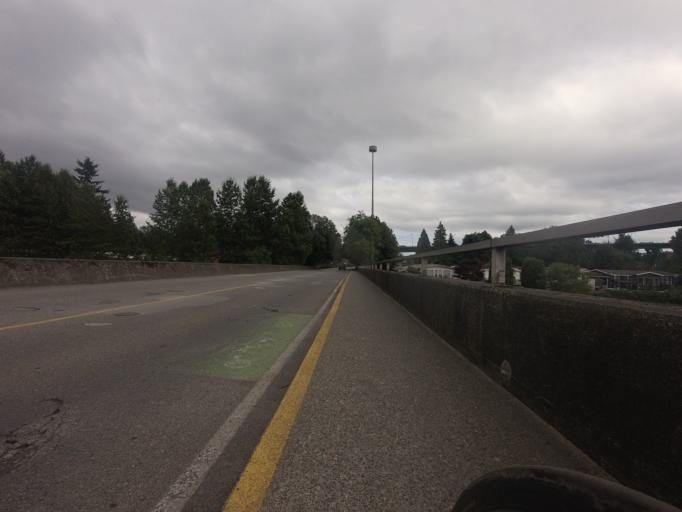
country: CA
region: British Columbia
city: West End
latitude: 49.3245
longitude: -123.1334
